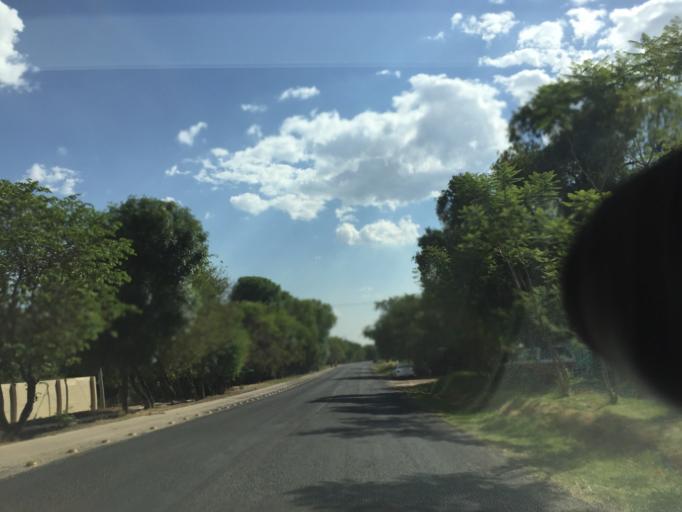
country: MX
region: Jalisco
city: Atotonilco el Alto
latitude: 20.5589
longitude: -102.4884
